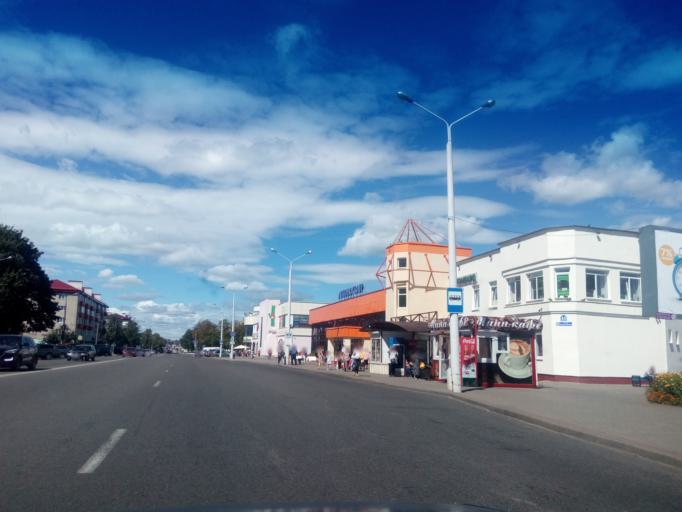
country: BY
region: Vitebsk
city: Polatsk
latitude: 55.4898
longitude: 28.7838
